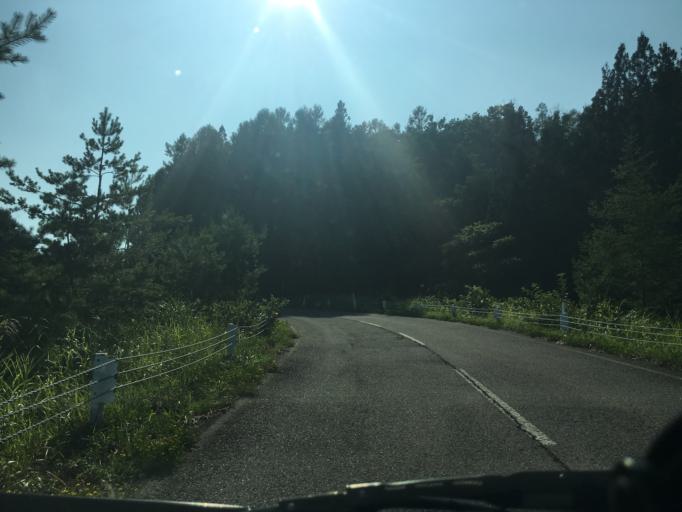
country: JP
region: Fukushima
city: Kitakata
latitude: 37.7399
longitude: 139.8727
